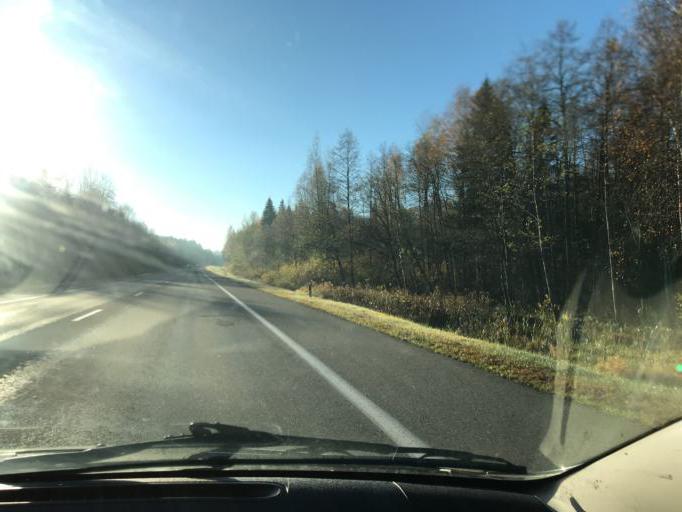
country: BY
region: Vitebsk
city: Vitebsk
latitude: 54.8943
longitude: 30.3811
